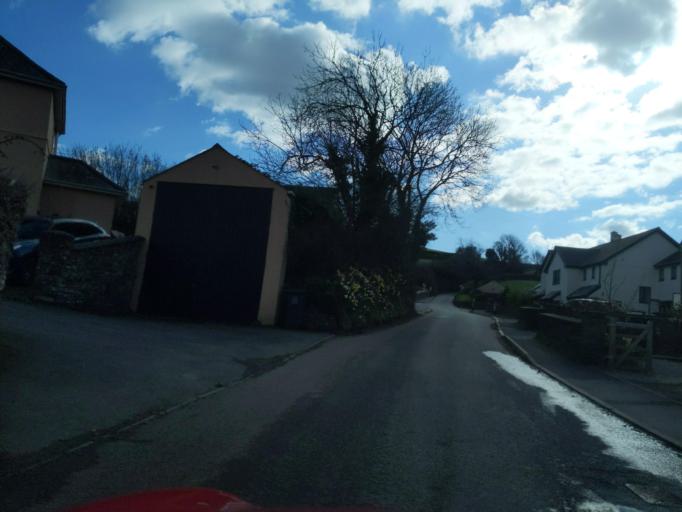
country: GB
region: England
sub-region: Devon
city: Kingsbridge
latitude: 50.2699
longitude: -3.7200
